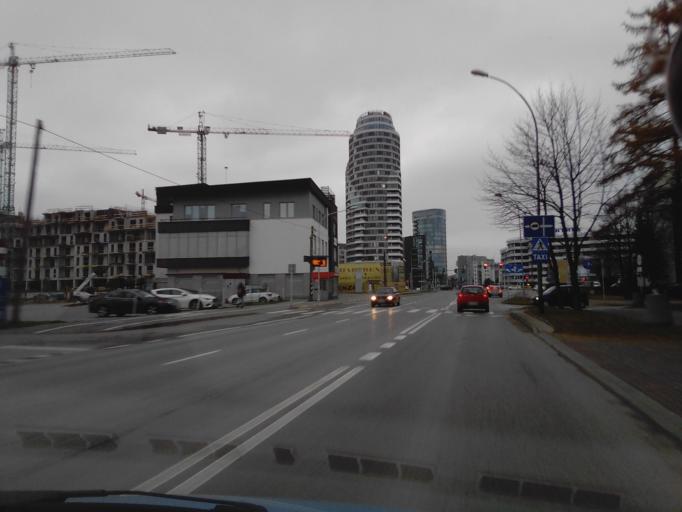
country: PL
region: Subcarpathian Voivodeship
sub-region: Rzeszow
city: Rzeszow
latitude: 50.0280
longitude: 22.0074
